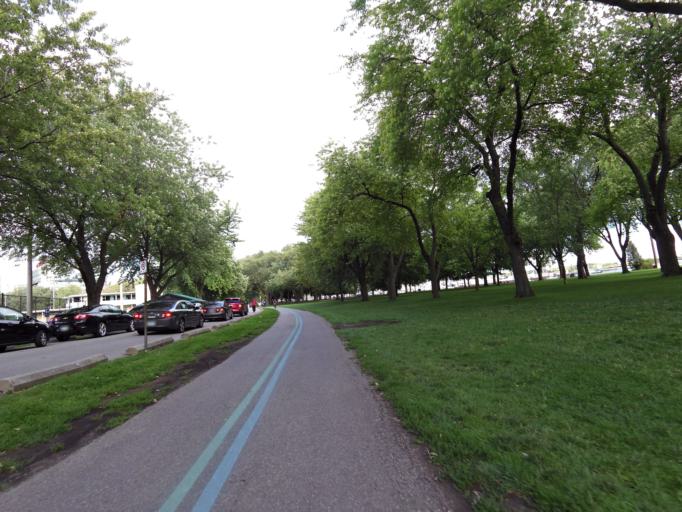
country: CA
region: Ontario
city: Toronto
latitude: 43.6341
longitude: -79.4064
